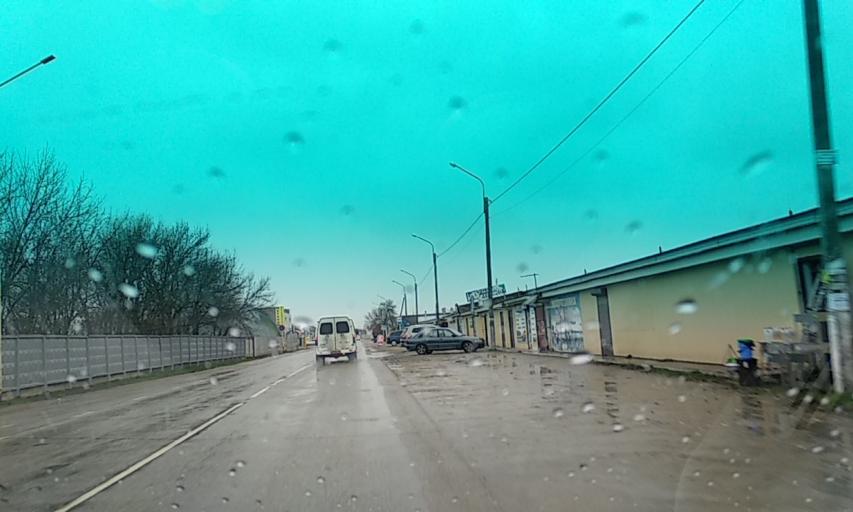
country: RU
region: Krasnodarskiy
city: Belorechensk
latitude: 44.7934
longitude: 39.8617
